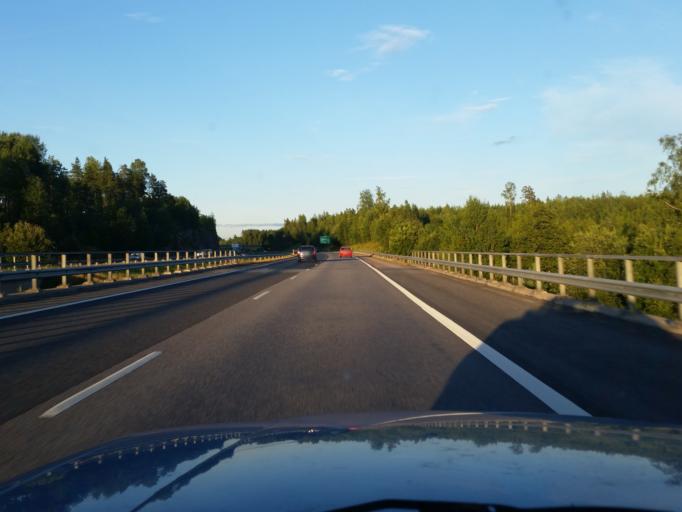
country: FI
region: Varsinais-Suomi
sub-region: Turku
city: Piikkioe
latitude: 60.4455
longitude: 22.5381
